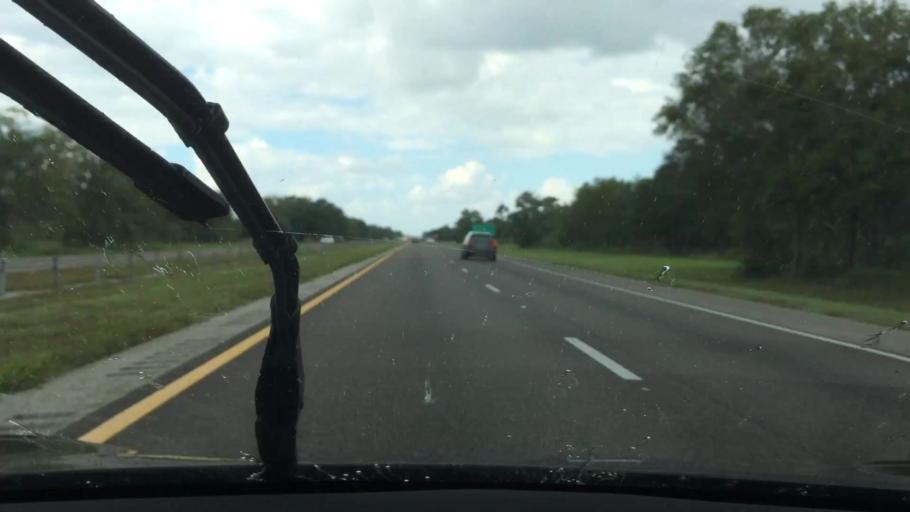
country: US
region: Florida
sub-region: Orange County
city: Wedgefield
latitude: 28.4516
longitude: -81.0783
